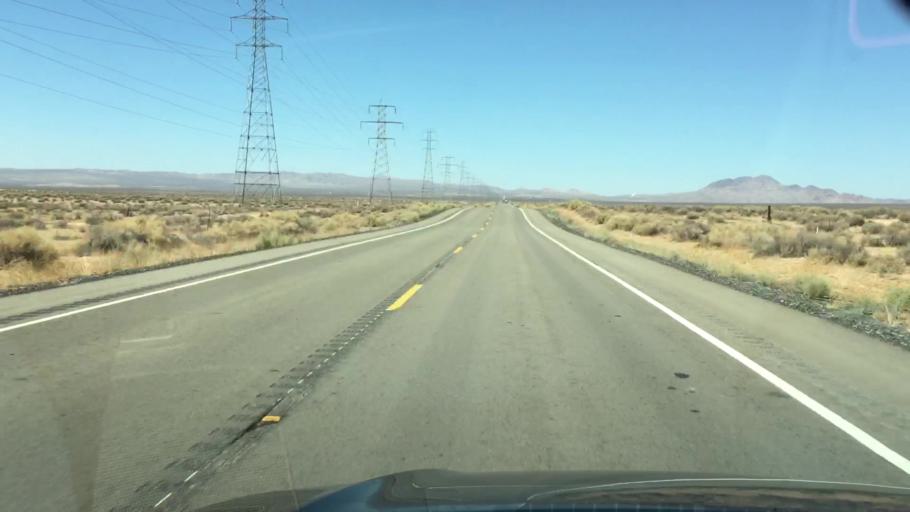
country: US
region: California
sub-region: Kern County
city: Boron
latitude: 35.1714
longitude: -117.5915
